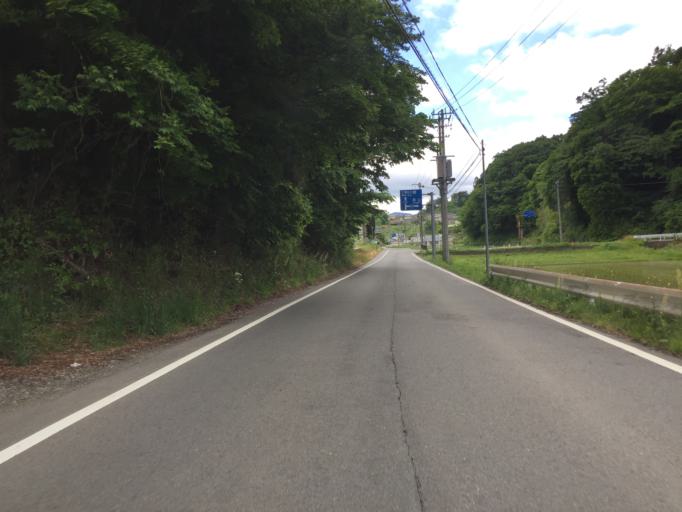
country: JP
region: Fukushima
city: Miharu
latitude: 37.4543
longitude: 140.4713
